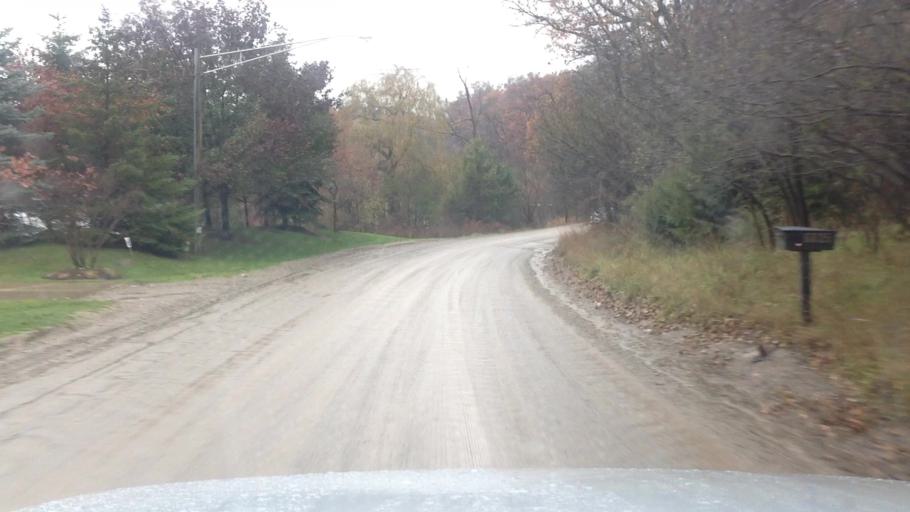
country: US
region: Michigan
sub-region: Oakland County
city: West Bloomfield Township
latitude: 42.5589
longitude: -83.4157
